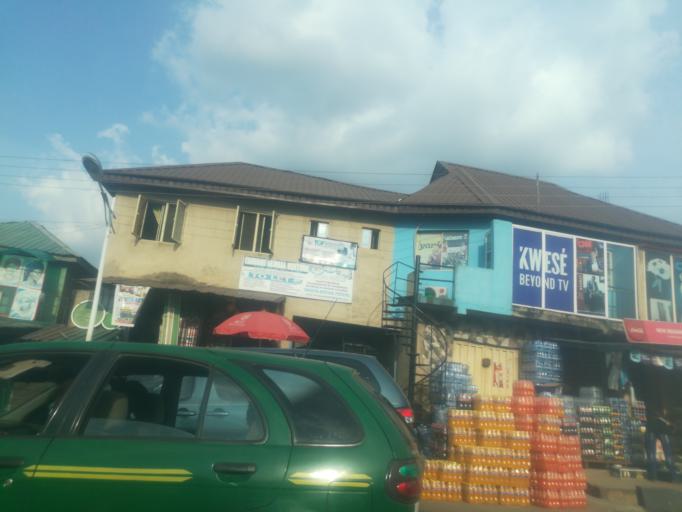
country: NG
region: Ogun
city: Abeokuta
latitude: 7.1459
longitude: 3.3301
